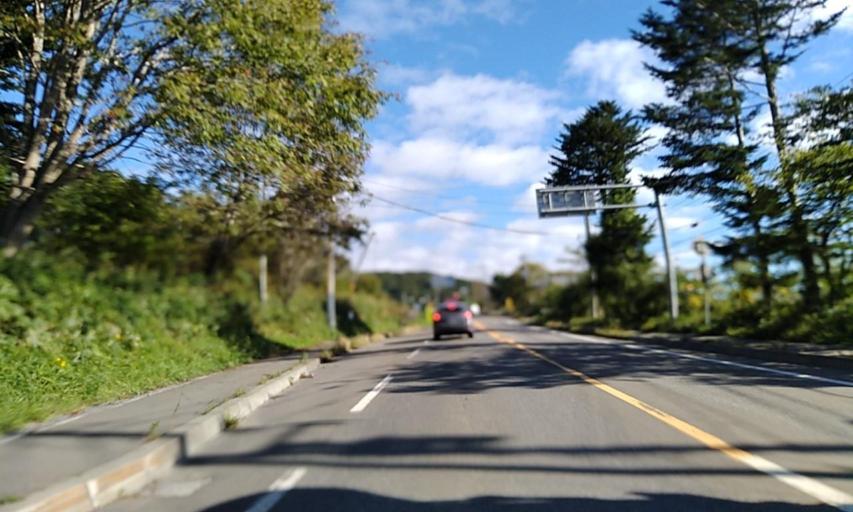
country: JP
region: Hokkaido
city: Shizunai-furukawacho
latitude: 42.3712
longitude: 142.3079
